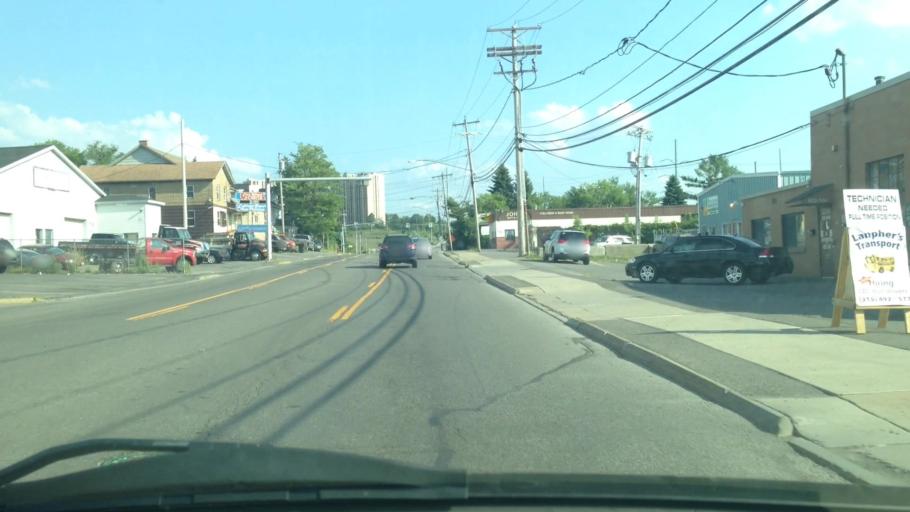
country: US
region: New York
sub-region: Onondaga County
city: Syracuse
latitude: 43.0127
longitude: -76.1348
